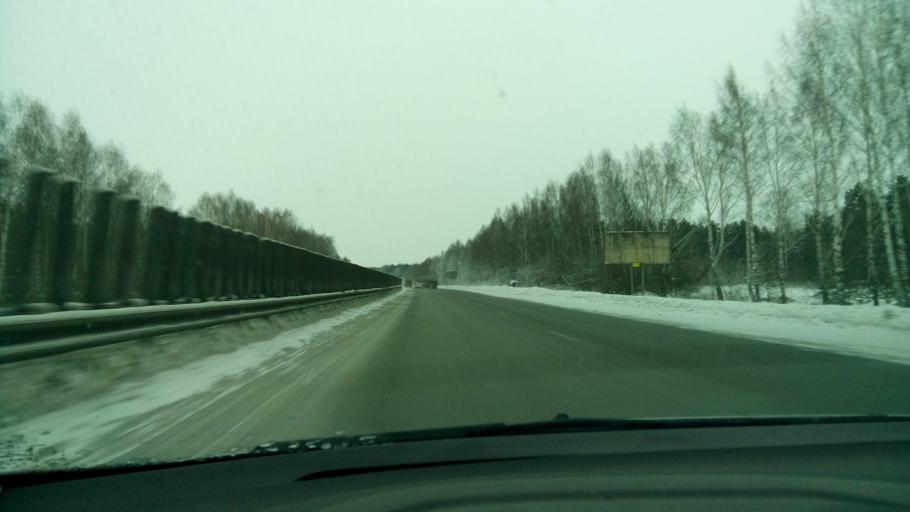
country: RU
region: Sverdlovsk
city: Istok
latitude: 56.7782
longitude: 60.8528
